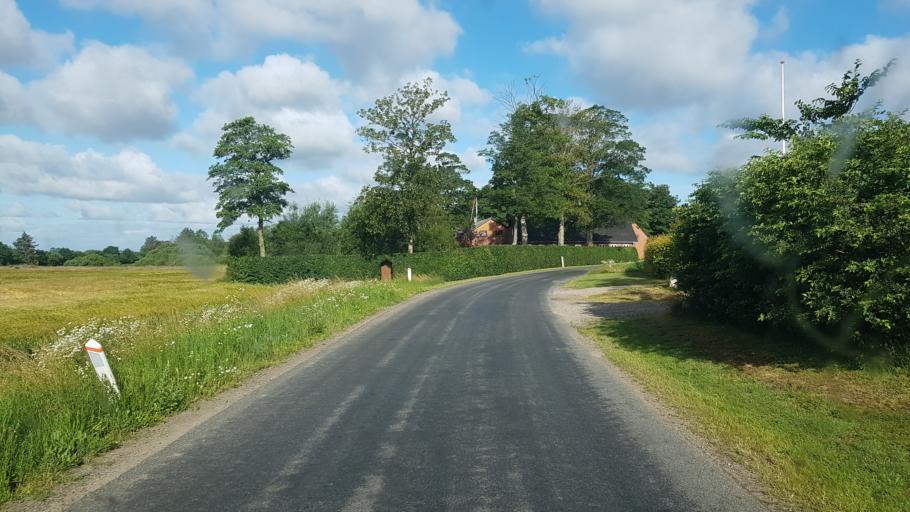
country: DK
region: South Denmark
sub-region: Vejen Kommune
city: Holsted
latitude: 55.4495
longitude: 8.8649
